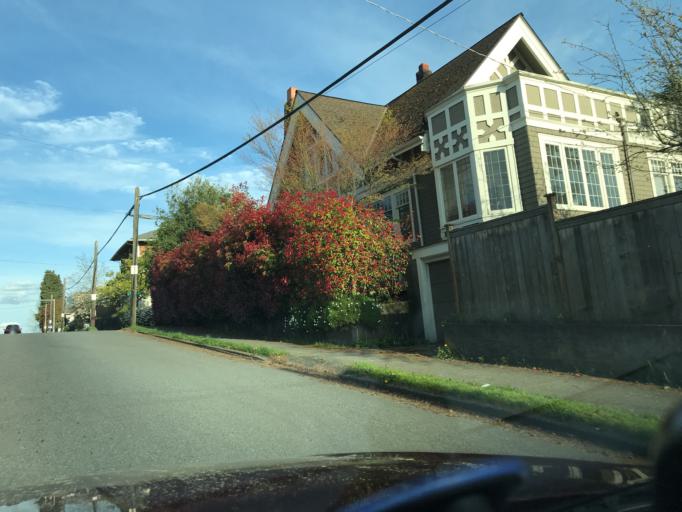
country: US
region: Washington
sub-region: King County
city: Seattle
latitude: 47.6758
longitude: -122.3105
